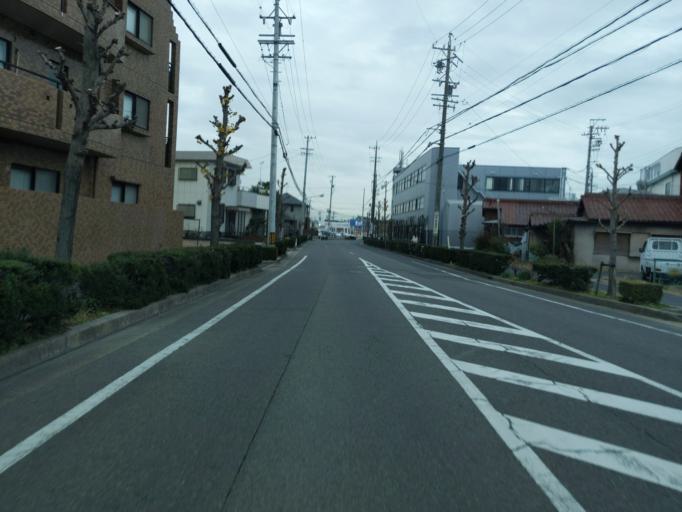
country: JP
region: Aichi
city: Kasugai
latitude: 35.2525
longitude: 136.9452
